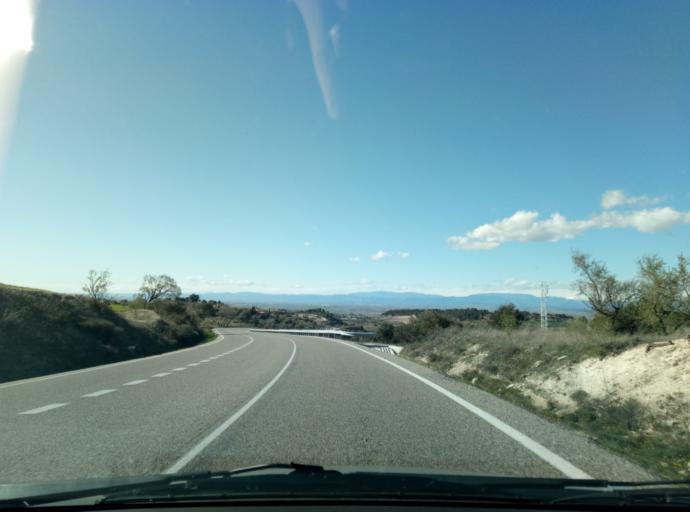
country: ES
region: Catalonia
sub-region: Provincia de Lleida
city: Ciutadilla
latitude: 41.5556
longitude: 1.1375
